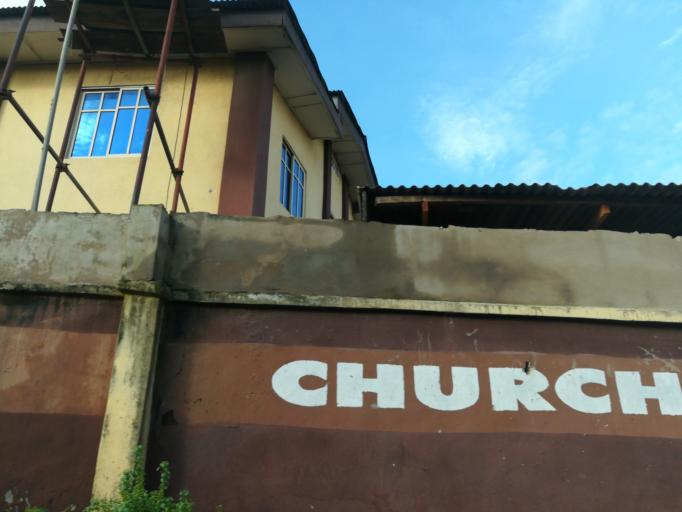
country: NG
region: Lagos
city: Oshodi
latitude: 6.5518
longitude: 3.3335
